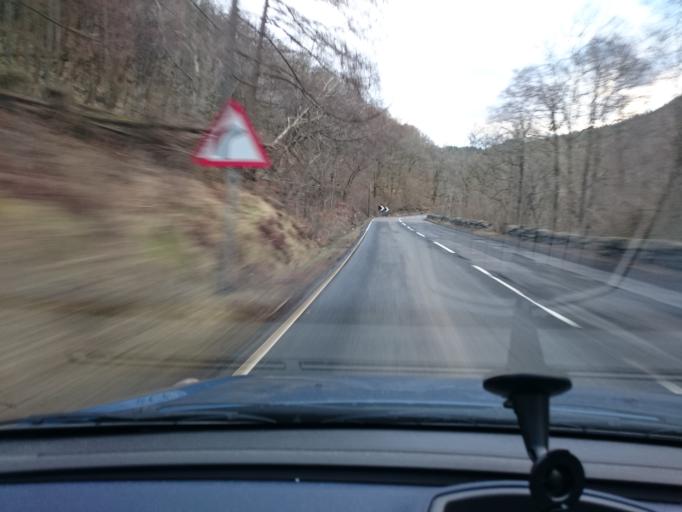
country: GB
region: Scotland
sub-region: Stirling
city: Callander
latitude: 56.2542
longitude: -4.2813
